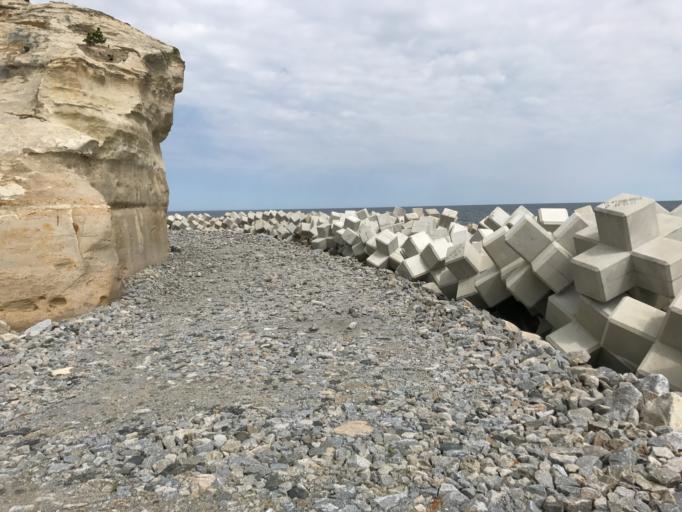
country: JP
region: Miyagi
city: Marumori
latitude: 37.8222
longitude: 140.9866
